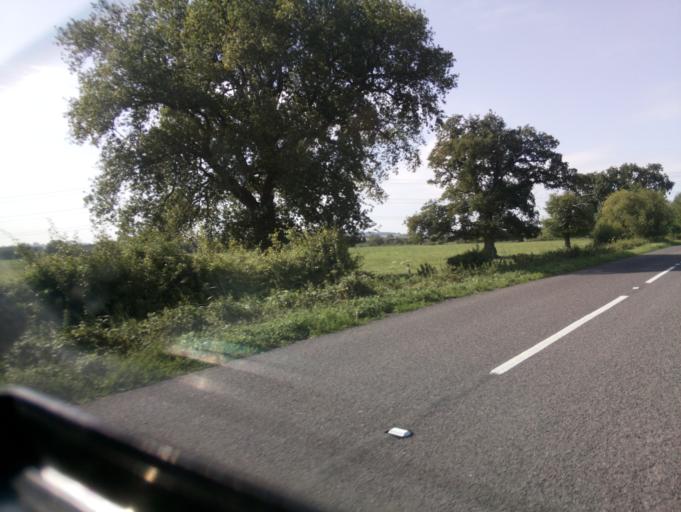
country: GB
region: England
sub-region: Oxfordshire
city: Faringdon
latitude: 51.6897
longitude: -1.5888
